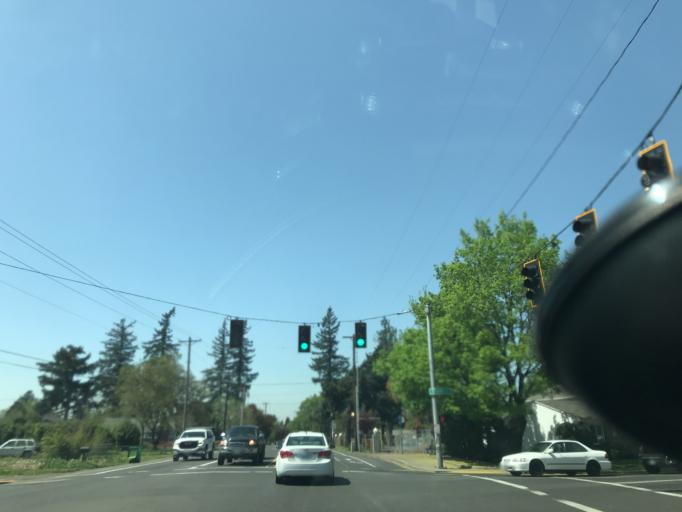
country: US
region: Oregon
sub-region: Clackamas County
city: Happy Valley
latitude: 45.4980
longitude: -122.5105
